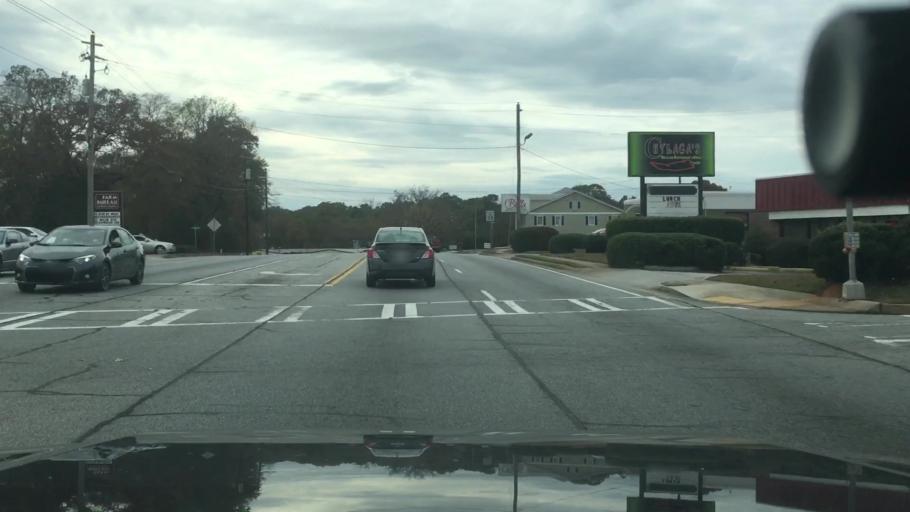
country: US
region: Georgia
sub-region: Coweta County
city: Newnan
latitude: 33.3828
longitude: -84.7910
